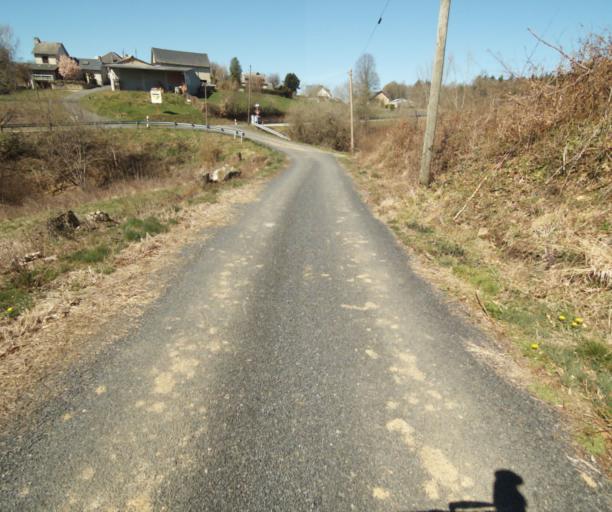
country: FR
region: Limousin
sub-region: Departement de la Correze
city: Chamboulive
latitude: 45.4410
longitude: 1.7254
